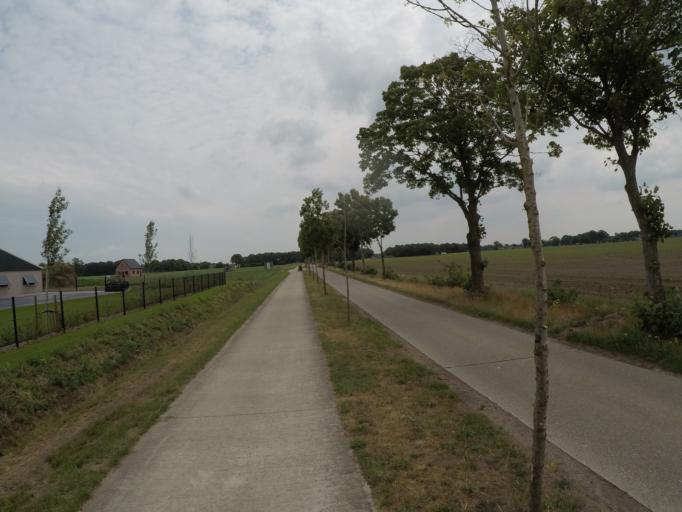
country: BE
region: Flanders
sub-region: Provincie Antwerpen
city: Wuustwezel
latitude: 51.4206
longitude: 4.5850
